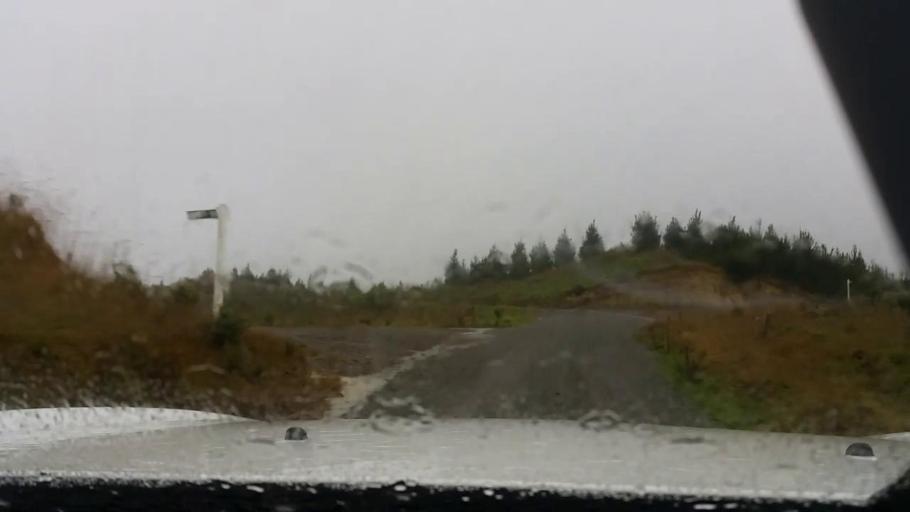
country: NZ
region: Wellington
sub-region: Masterton District
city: Masterton
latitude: -41.1926
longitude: 175.8105
